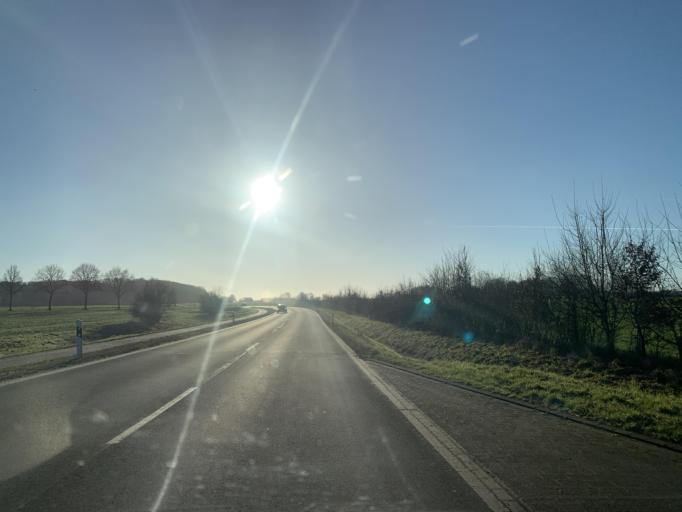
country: DE
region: North Rhine-Westphalia
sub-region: Regierungsbezirk Munster
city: Dulmen
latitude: 51.8664
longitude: 7.2868
